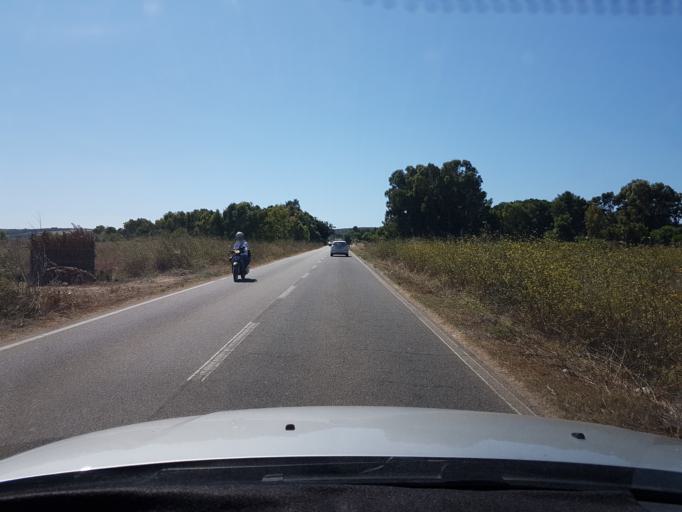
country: IT
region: Sardinia
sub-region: Provincia di Oristano
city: Cabras
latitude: 39.9158
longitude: 8.4597
